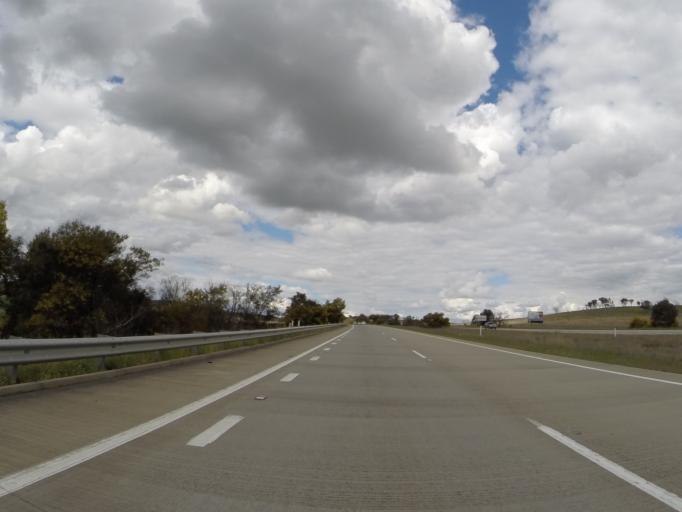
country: AU
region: New South Wales
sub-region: Yass Valley
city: Gundaroo
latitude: -34.7964
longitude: 149.2771
